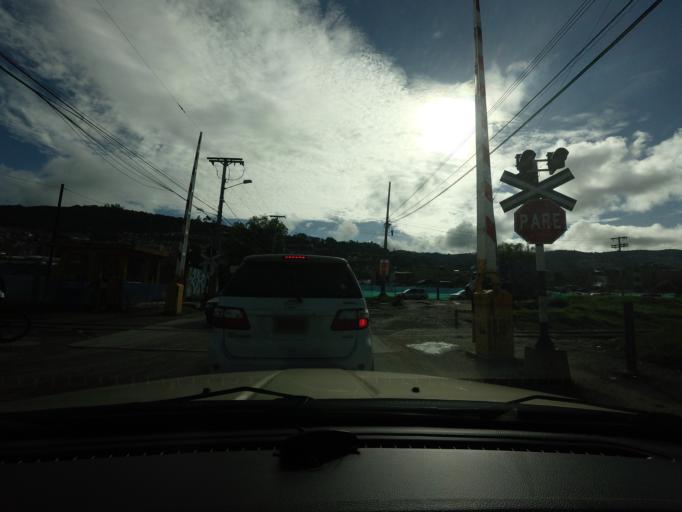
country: CO
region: Cundinamarca
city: La Calera
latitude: 4.7603
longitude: -74.0314
